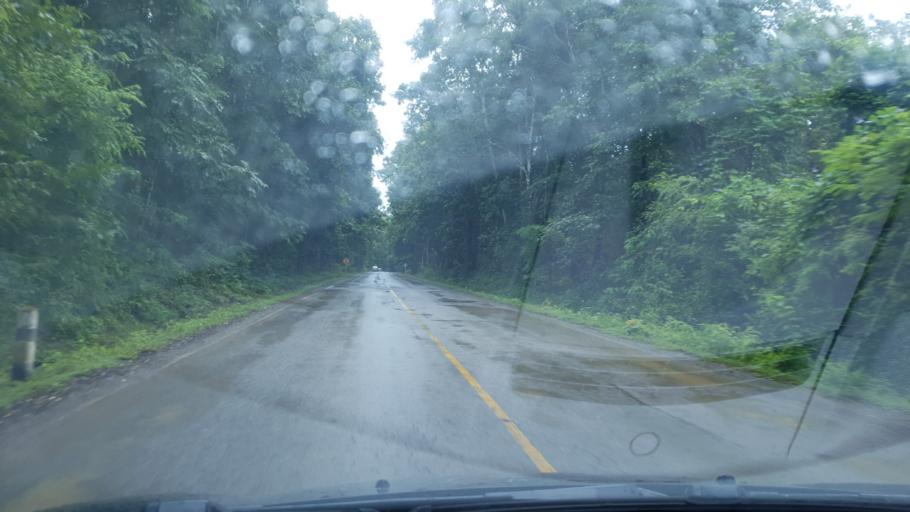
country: TH
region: Mae Hong Son
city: Pa Pae
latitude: 18.2508
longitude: 97.9434
